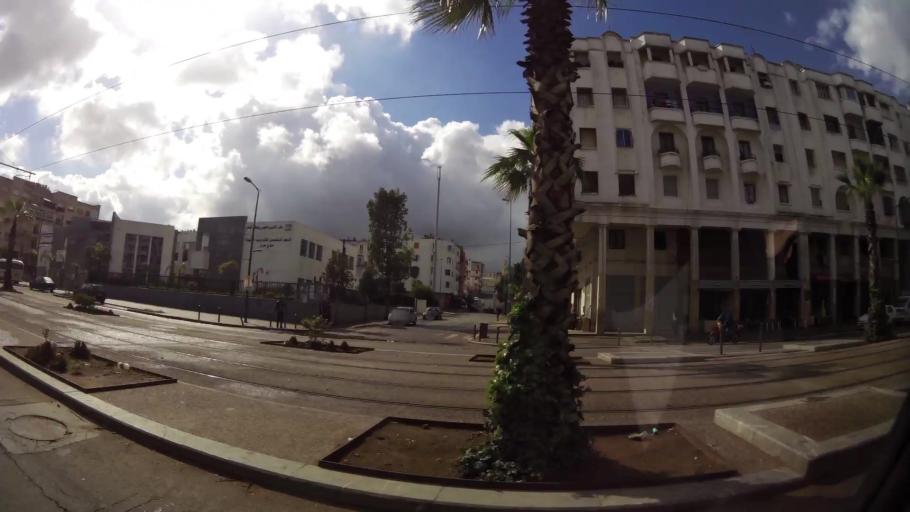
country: MA
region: Grand Casablanca
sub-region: Mediouna
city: Tit Mellil
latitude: 33.5747
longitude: -7.5227
